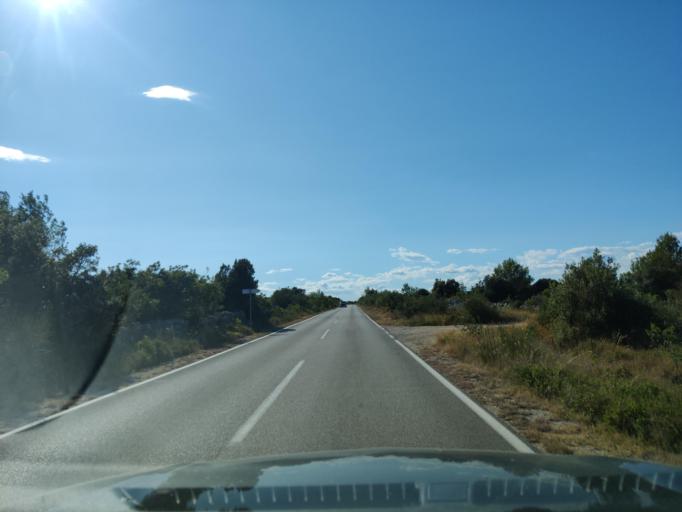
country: HR
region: Sibensko-Kniniska
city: Zaton
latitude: 43.7434
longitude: 15.8511
